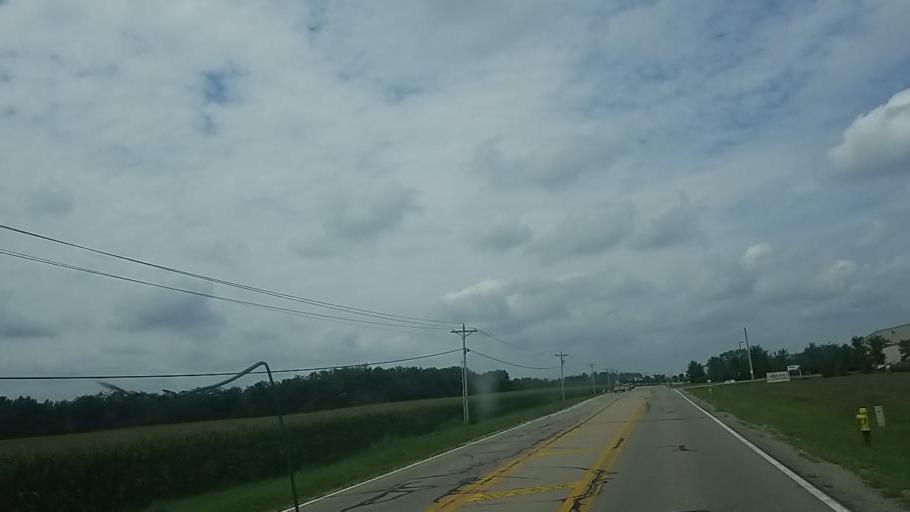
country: US
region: Ohio
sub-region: Franklin County
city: Groveport
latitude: 39.8300
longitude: -82.9025
